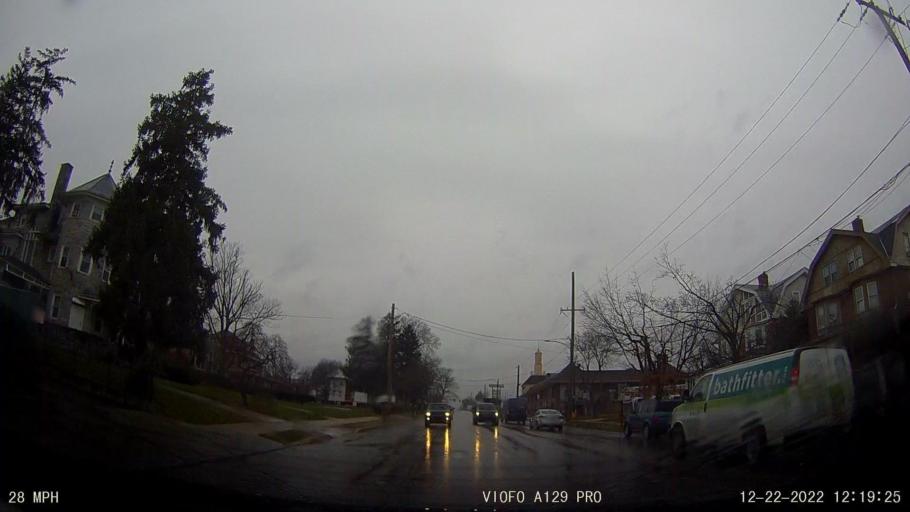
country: US
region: Pennsylvania
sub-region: Montgomery County
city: West Norriton
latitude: 40.1221
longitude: -75.3601
